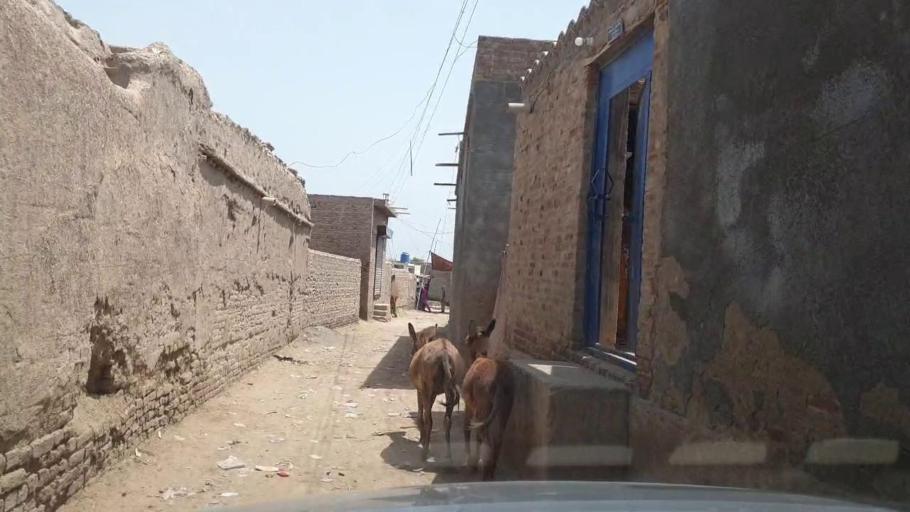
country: PK
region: Sindh
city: Madeji
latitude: 27.7597
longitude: 68.3836
